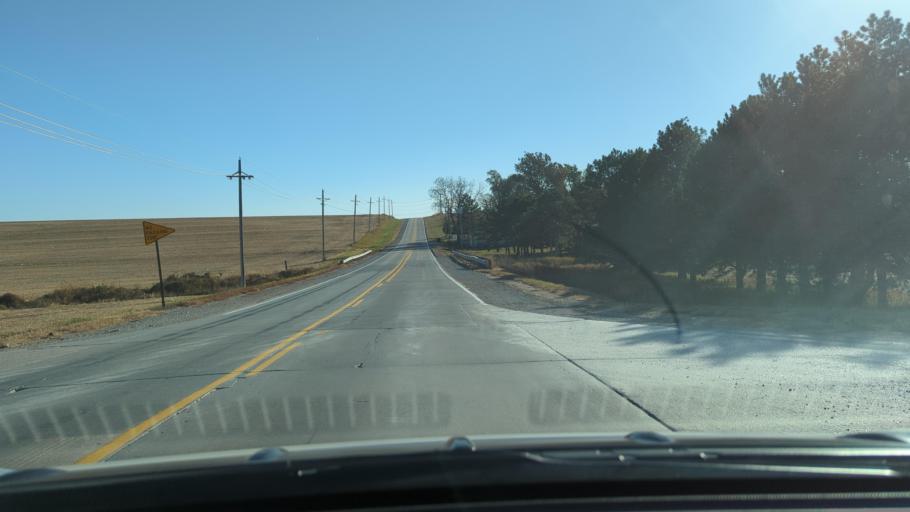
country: US
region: Nebraska
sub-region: Sarpy County
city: Papillion
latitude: 41.0927
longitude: -96.0093
